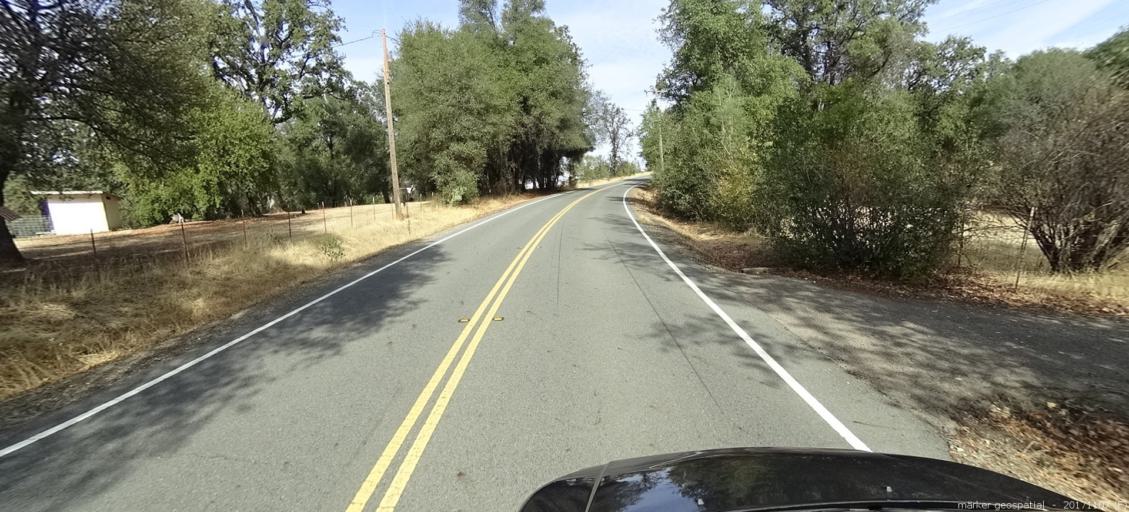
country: US
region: California
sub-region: Shasta County
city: Shasta
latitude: 40.4963
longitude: -122.5466
